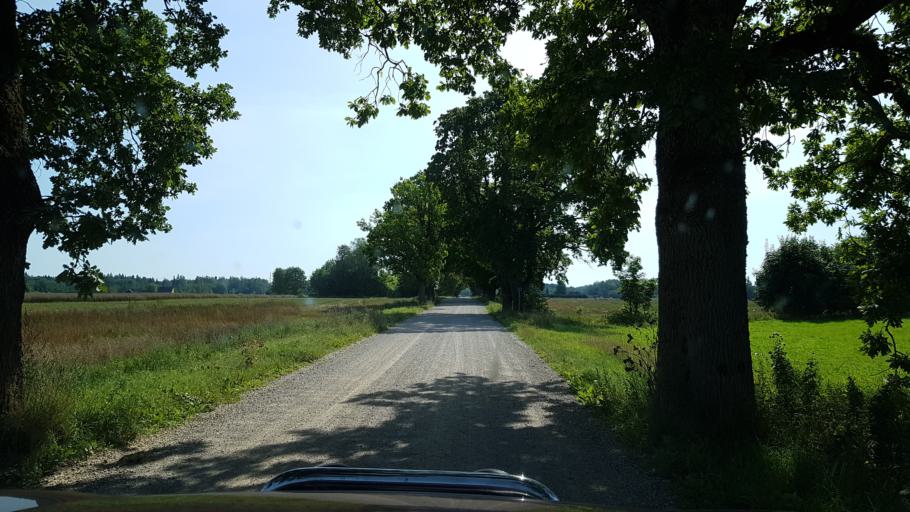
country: EE
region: Viljandimaa
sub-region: Suure-Jaani vald
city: Suure-Jaani
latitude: 58.4805
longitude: 25.5229
